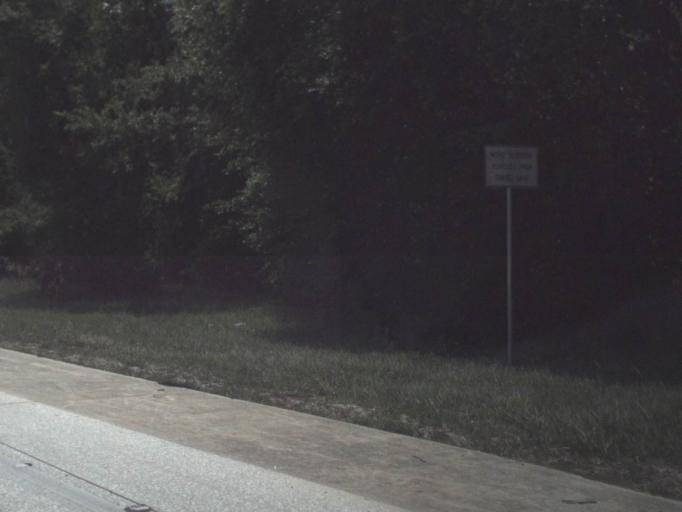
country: US
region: Florida
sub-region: Saint Johns County
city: Fruit Cove
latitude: 30.2111
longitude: -81.5651
